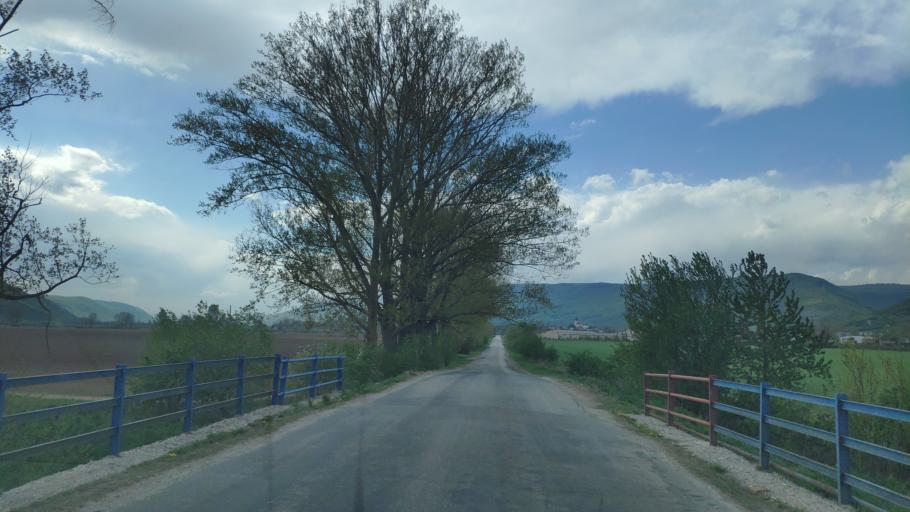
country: SK
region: Kosicky
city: Medzev
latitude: 48.5937
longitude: 20.8939
